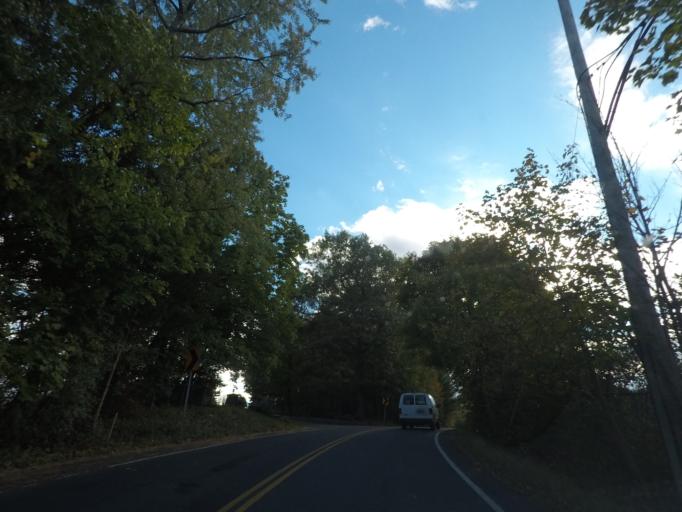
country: US
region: New York
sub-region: Schenectady County
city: Niskayuna
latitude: 42.7641
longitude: -73.8297
